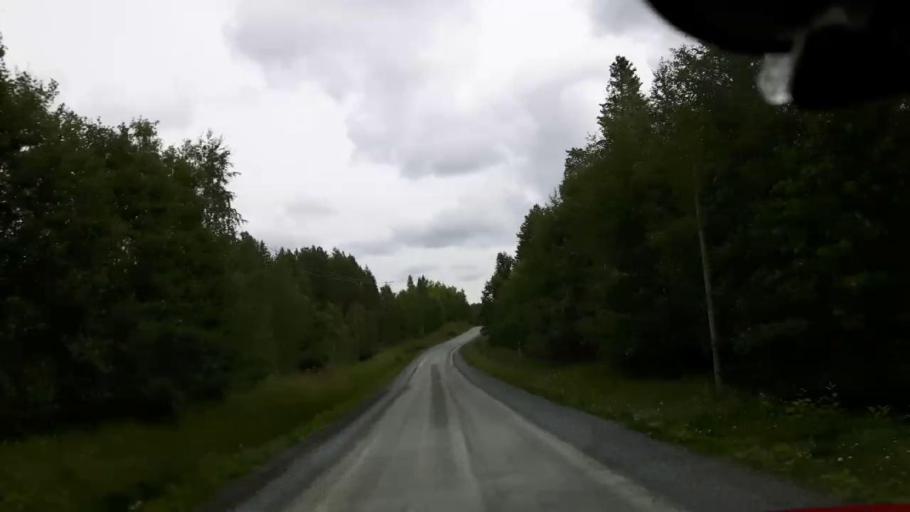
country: SE
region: Jaemtland
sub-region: Krokoms Kommun
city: Krokom
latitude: 63.5794
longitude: 14.2053
